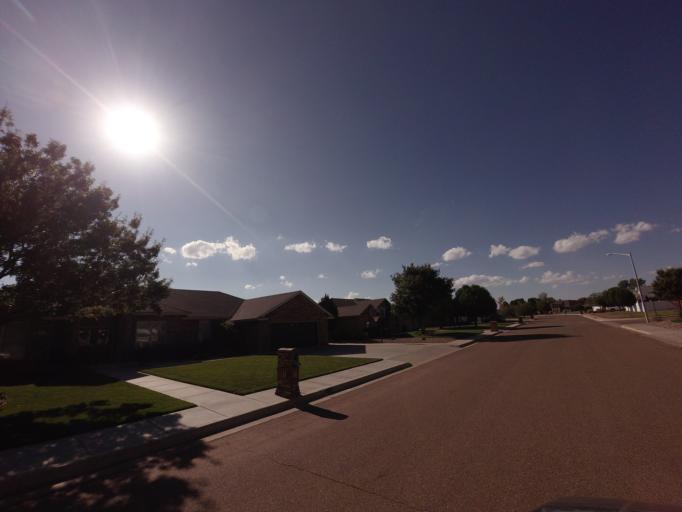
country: US
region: New Mexico
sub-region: Curry County
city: Clovis
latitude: 34.4398
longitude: -103.1746
